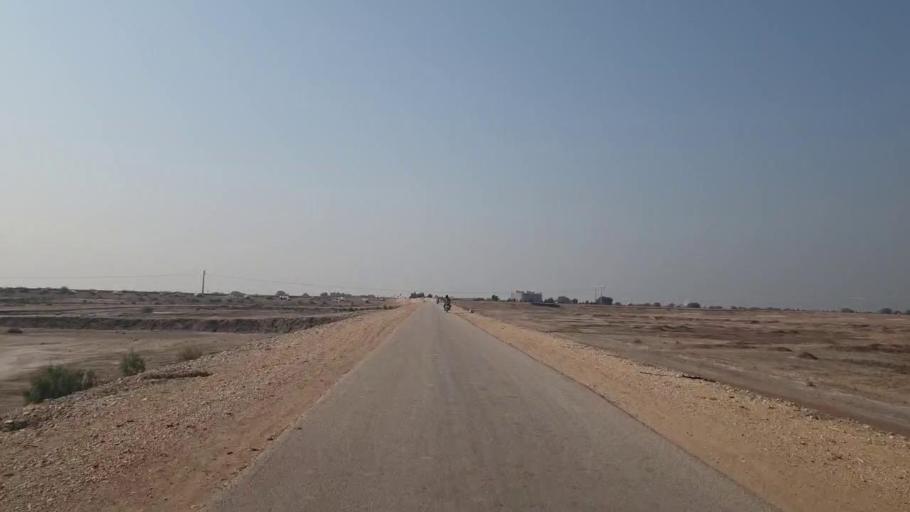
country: PK
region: Sindh
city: Sehwan
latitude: 26.4316
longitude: 67.8423
